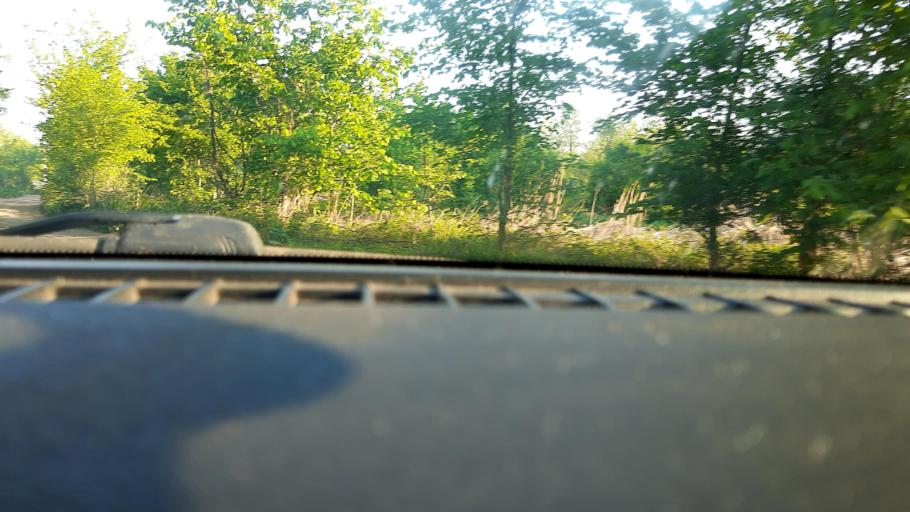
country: RU
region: Bashkortostan
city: Iglino
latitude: 54.7729
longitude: 56.2119
